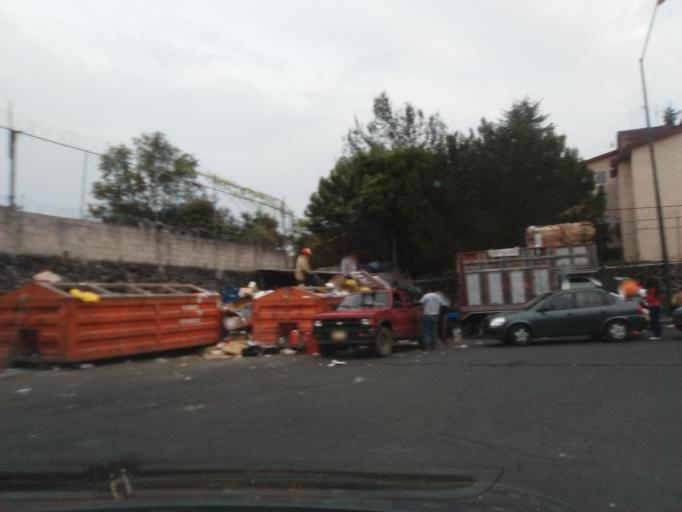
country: MX
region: Mexico City
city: Magdalena Contreras
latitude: 19.3061
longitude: -99.2170
